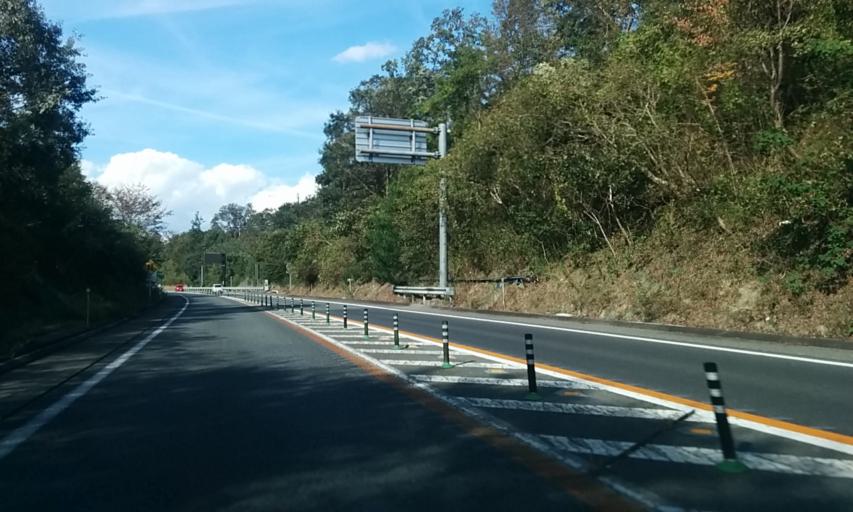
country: JP
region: Kyoto
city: Tanabe
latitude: 34.7798
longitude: 135.7732
